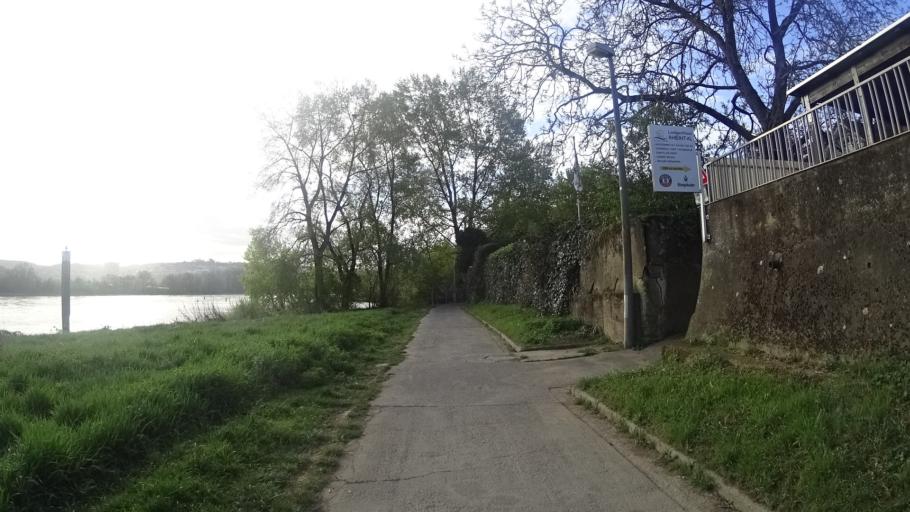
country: DE
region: Rheinland-Pfalz
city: Weitersburg
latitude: 50.3974
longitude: 7.5888
